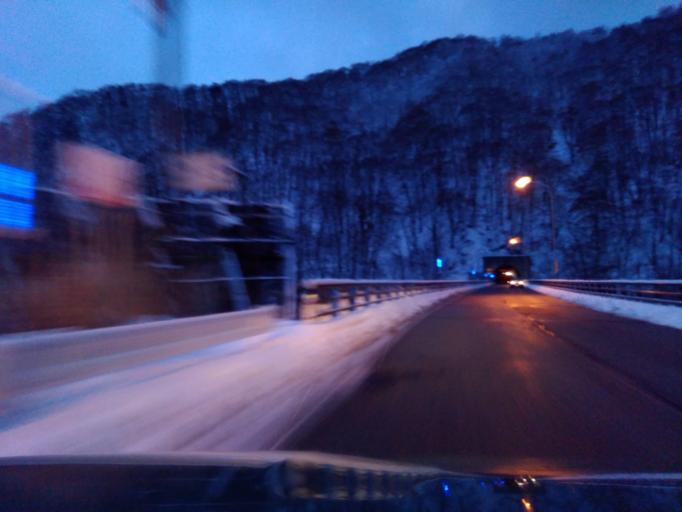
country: JP
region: Iwate
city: Shizukuishi
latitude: 39.6883
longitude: 140.7925
